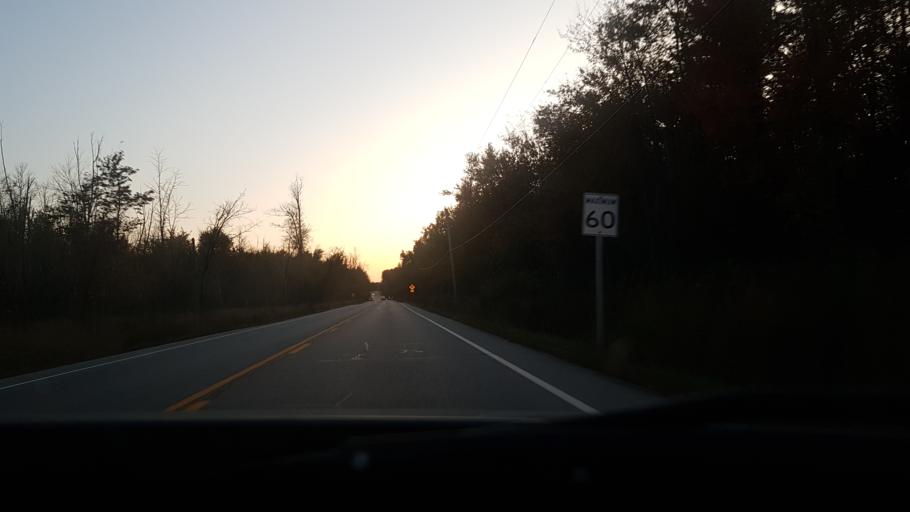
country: CA
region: Ontario
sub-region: Halton
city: Milton
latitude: 43.4686
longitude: -80.0004
